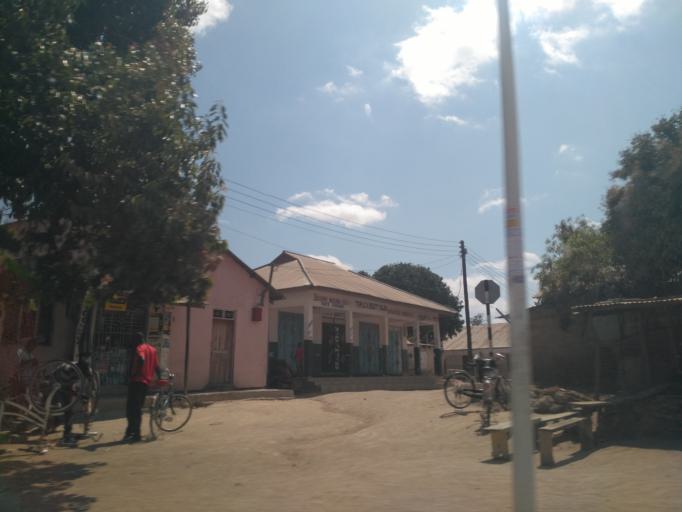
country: TZ
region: Dodoma
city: Dodoma
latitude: -6.1531
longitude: 35.7391
